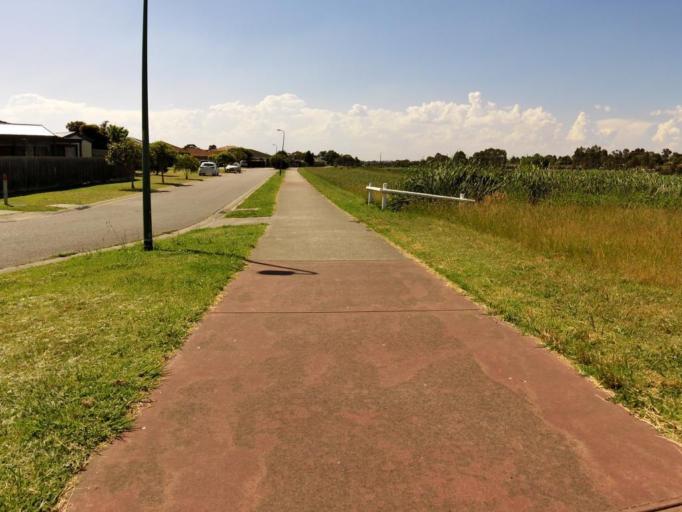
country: AU
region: Victoria
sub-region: Casey
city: Narre Warren South
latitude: -38.0476
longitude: 145.2779
